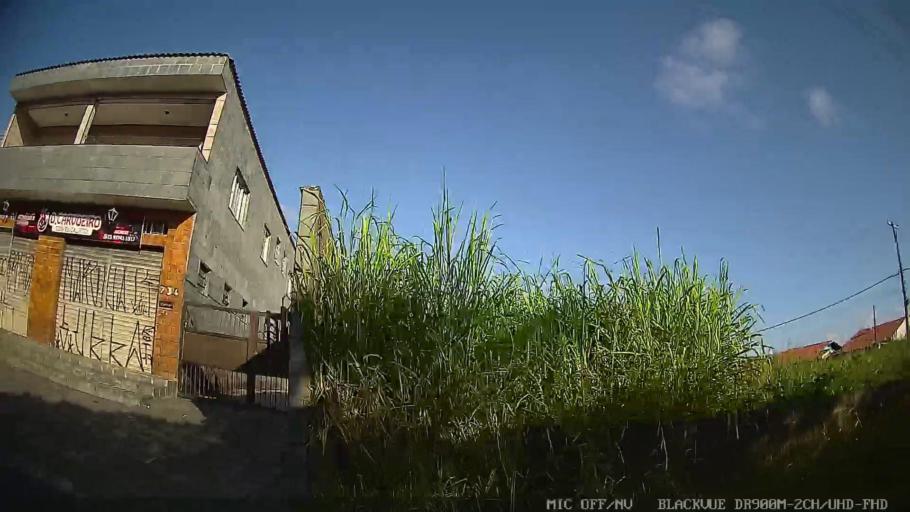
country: BR
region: Sao Paulo
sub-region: Peruibe
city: Peruibe
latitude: -24.2845
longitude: -46.9642
